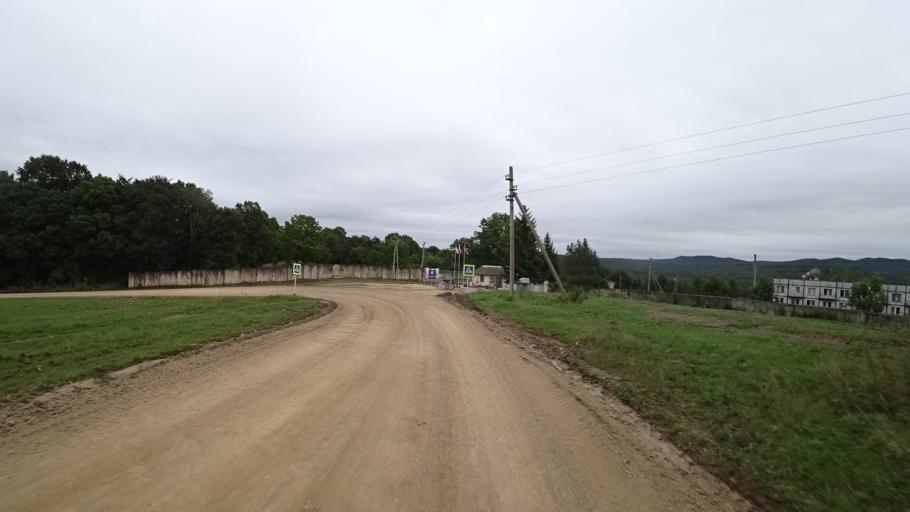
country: RU
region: Primorskiy
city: Rettikhovka
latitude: 44.1755
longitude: 132.8505
